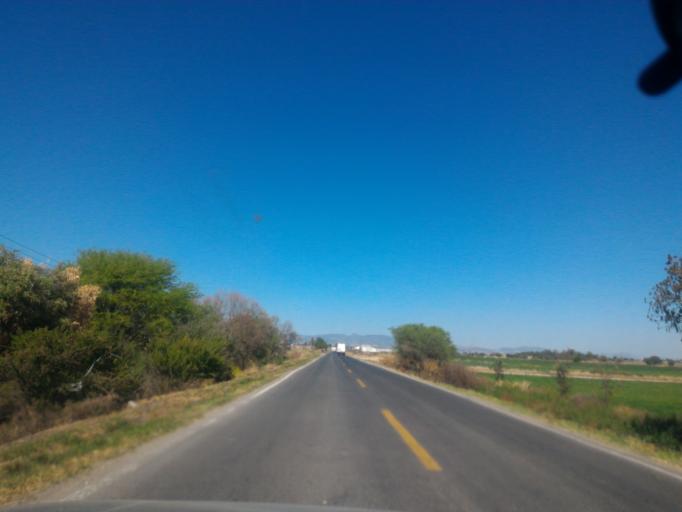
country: MX
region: Guanajuato
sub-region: San Francisco del Rincon
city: San Roque de Montes
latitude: 21.0186
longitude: -101.7927
